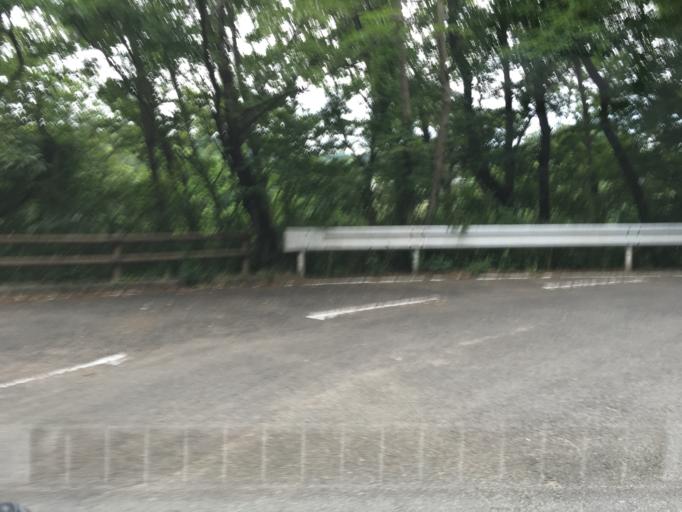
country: JP
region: Fukushima
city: Nihommatsu
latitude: 37.6359
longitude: 140.5260
